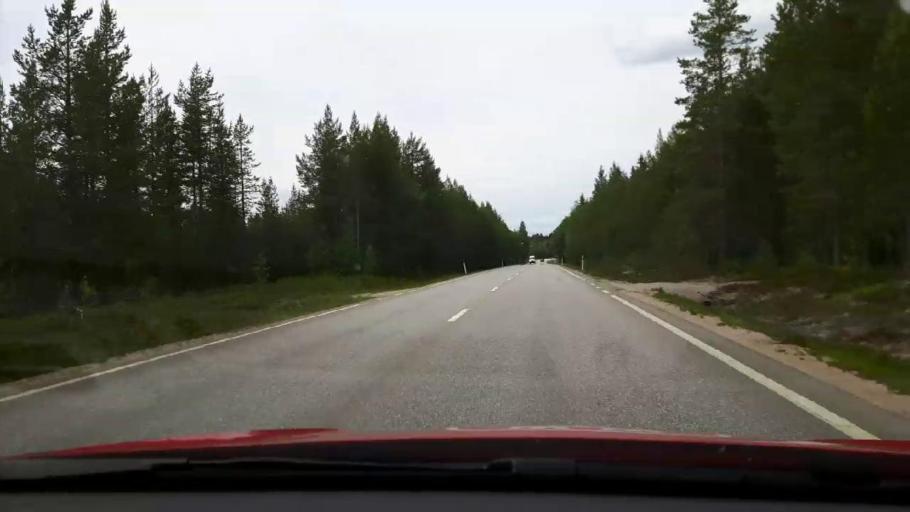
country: SE
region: Jaemtland
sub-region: Harjedalens Kommun
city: Sveg
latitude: 62.0612
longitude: 14.2850
